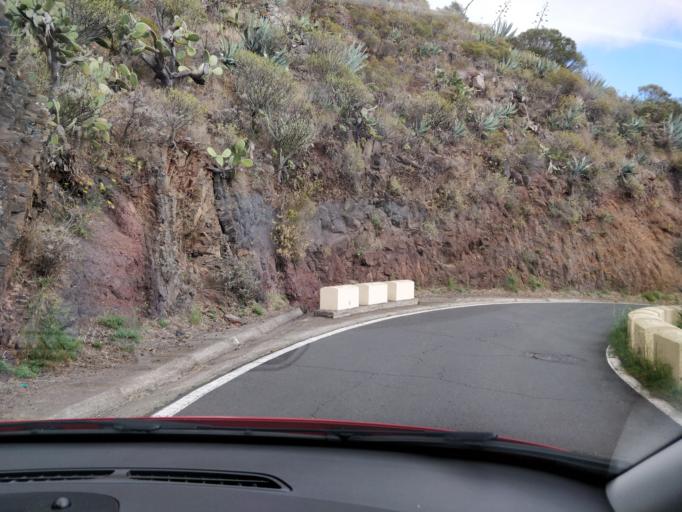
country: ES
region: Canary Islands
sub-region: Provincia de Santa Cruz de Tenerife
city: Santiago del Teide
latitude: 28.3221
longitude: -16.8560
